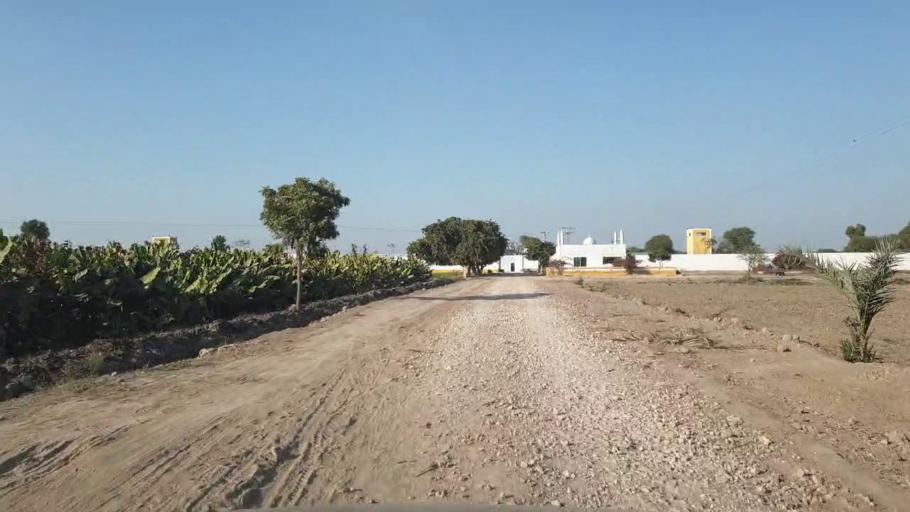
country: PK
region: Sindh
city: Tando Allahyar
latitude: 25.3866
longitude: 68.6840
